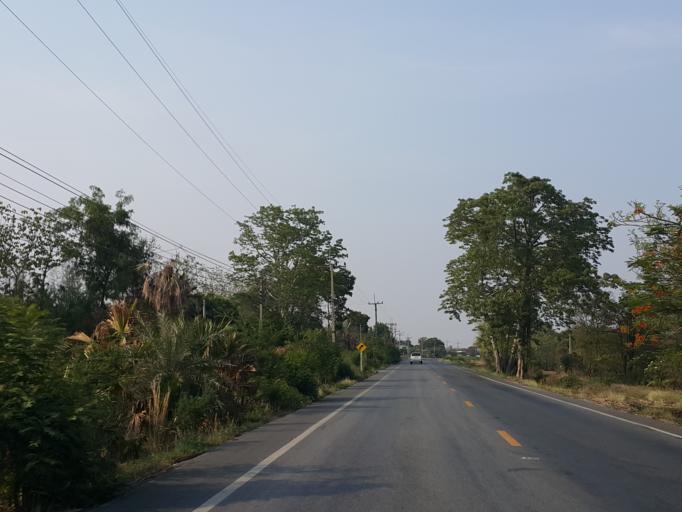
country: TH
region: Chai Nat
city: Hankha
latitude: 14.9673
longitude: 100.0962
